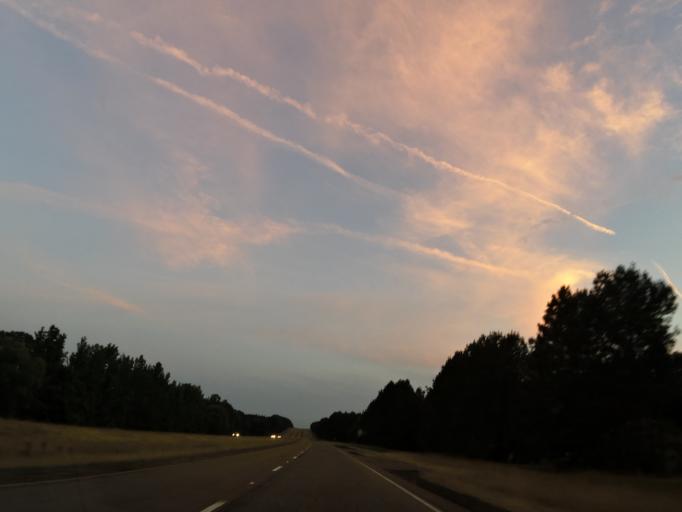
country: US
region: Mississippi
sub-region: Lauderdale County
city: Meridian Station
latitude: 32.5913
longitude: -88.5016
